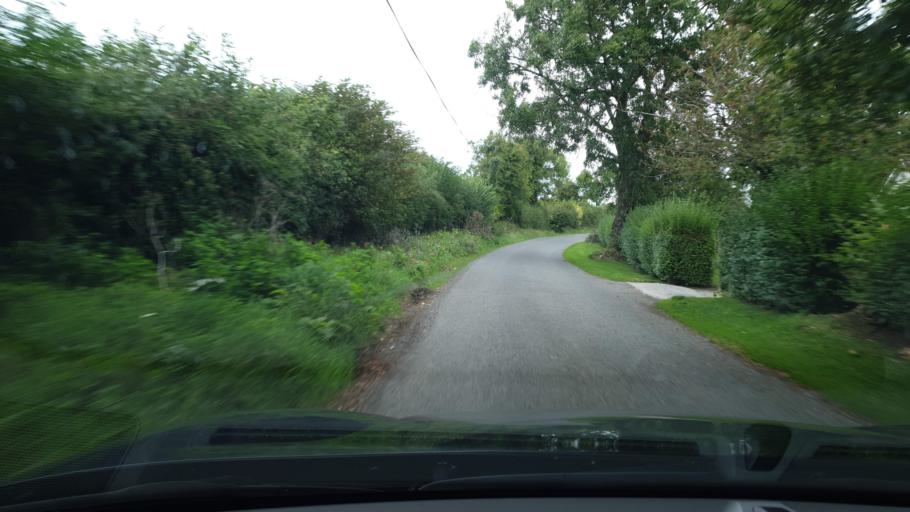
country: IE
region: Leinster
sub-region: An Mhi
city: Dunshaughlin
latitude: 53.5575
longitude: -6.5153
